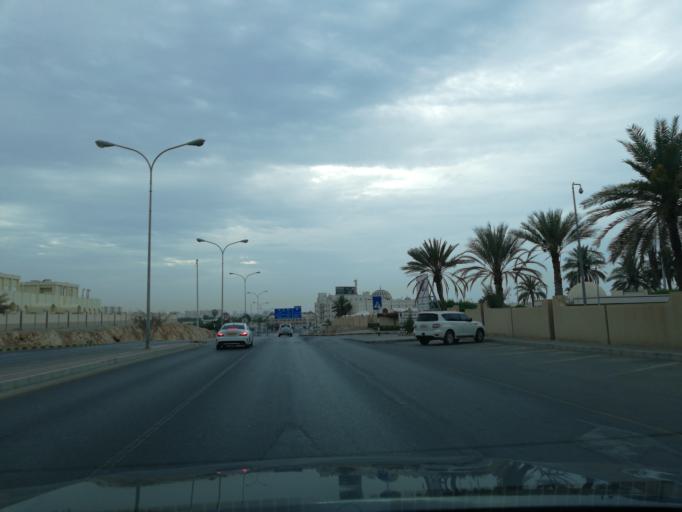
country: OM
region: Muhafazat Masqat
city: Bawshar
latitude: 23.5742
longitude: 58.3869
